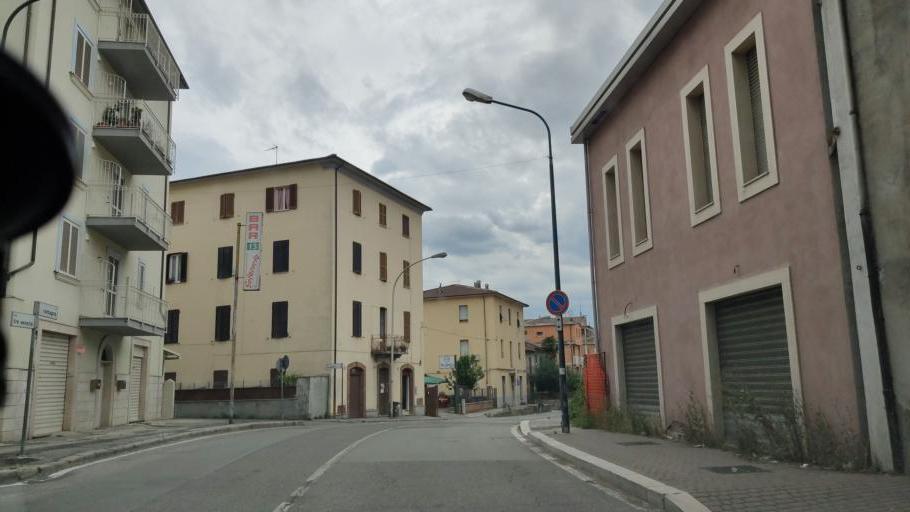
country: IT
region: Umbria
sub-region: Provincia di Terni
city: Terni
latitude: 42.5704
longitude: 12.6669
